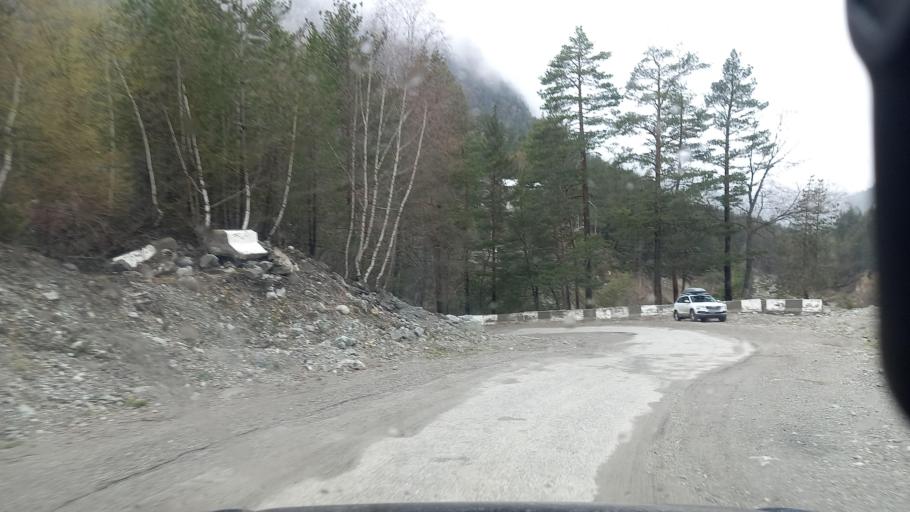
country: RU
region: Kabardino-Balkariya
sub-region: El'brusskiy Rayon
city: El'brus
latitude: 43.2288
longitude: 42.6561
